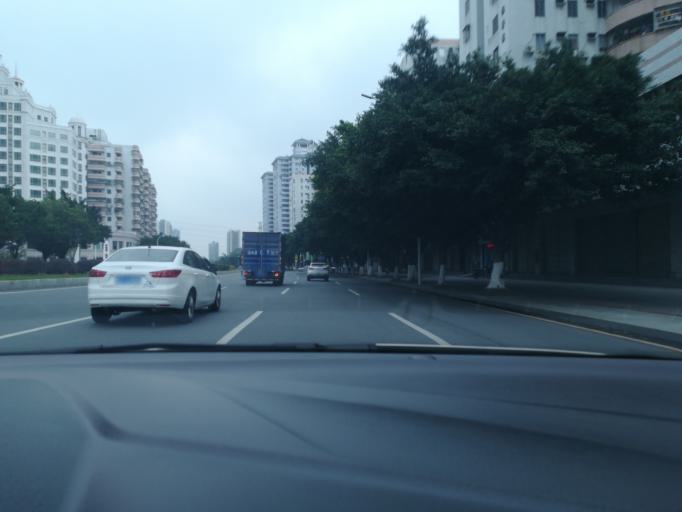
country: CN
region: Guangdong
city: Nansha
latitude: 22.8008
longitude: 113.5542
